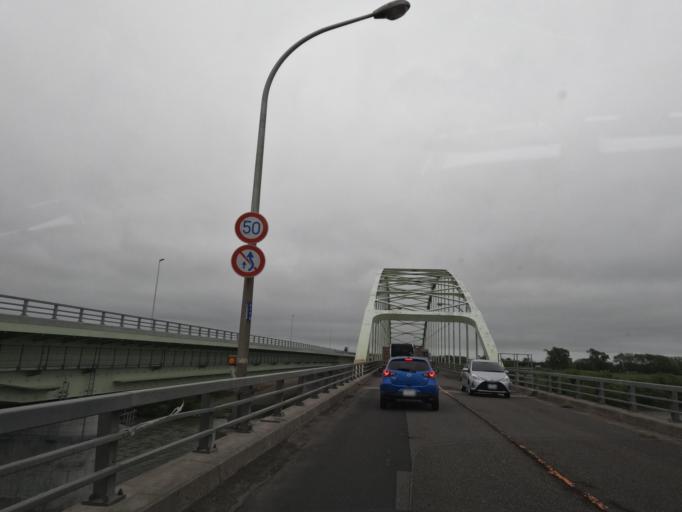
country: JP
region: Hokkaido
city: Ebetsu
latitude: 43.1357
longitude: 141.5115
